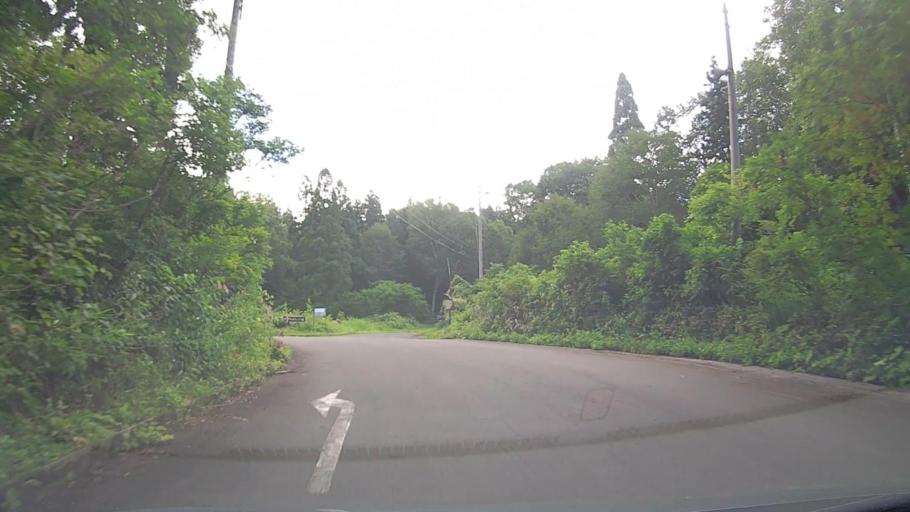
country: JP
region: Nagano
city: Iiyama
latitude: 36.9179
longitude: 138.4824
